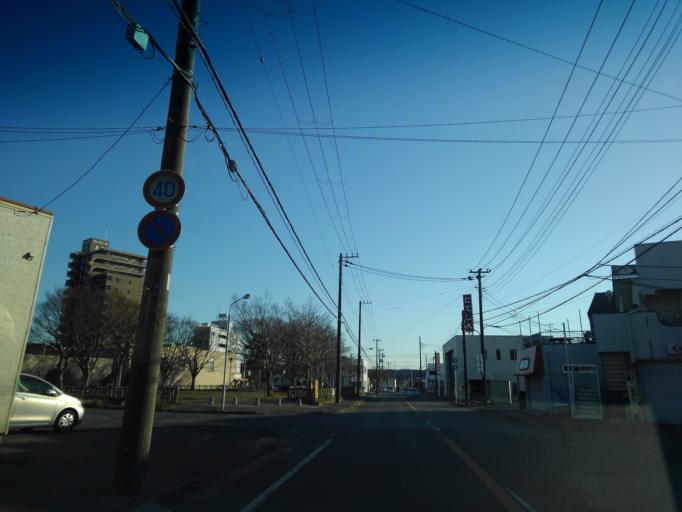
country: JP
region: Chiba
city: Kimitsu
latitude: 35.3309
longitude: 139.8995
